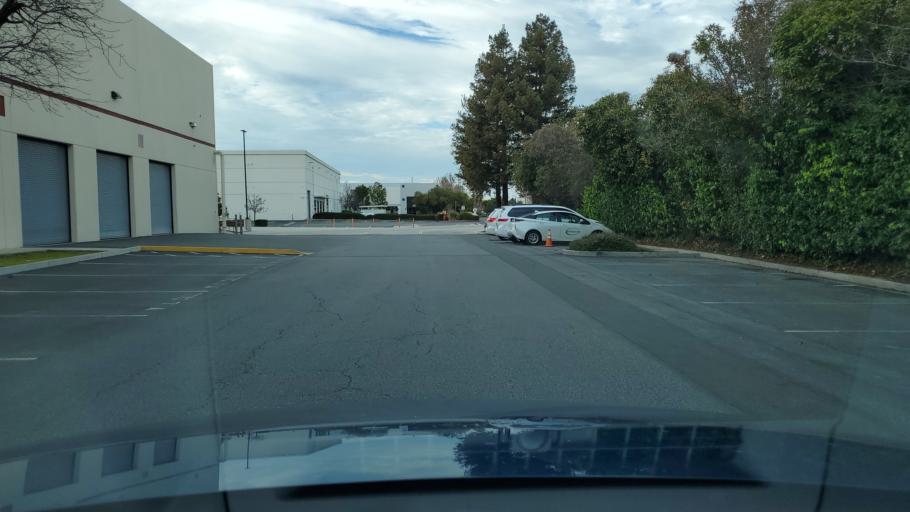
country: US
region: California
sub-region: Santa Clara County
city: Milpitas
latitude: 37.3888
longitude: -121.9033
